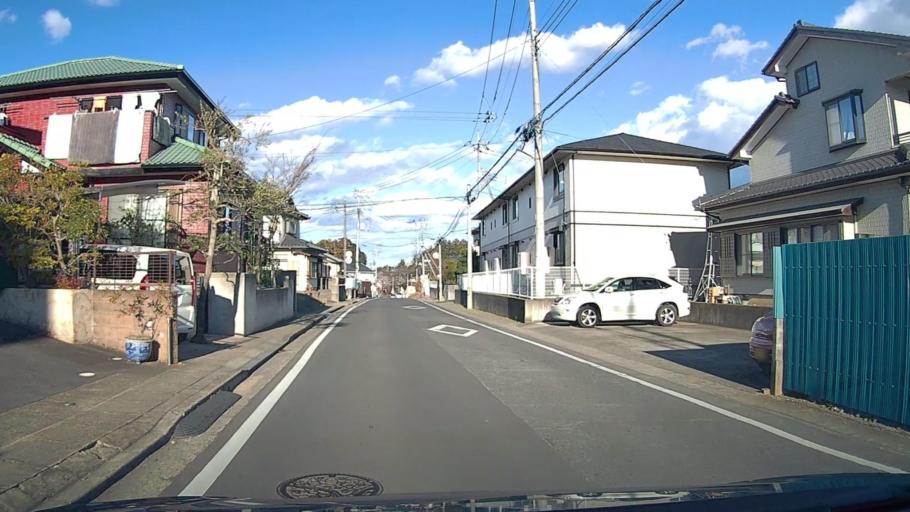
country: JP
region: Ibaraki
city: Mito-shi
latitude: 36.3727
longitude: 140.4431
